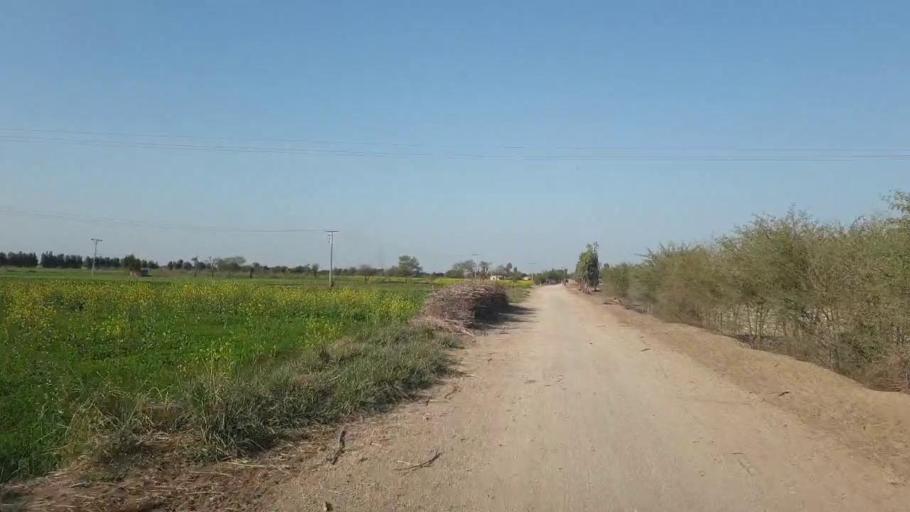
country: PK
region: Sindh
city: Tando Allahyar
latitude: 25.3908
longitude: 68.6990
